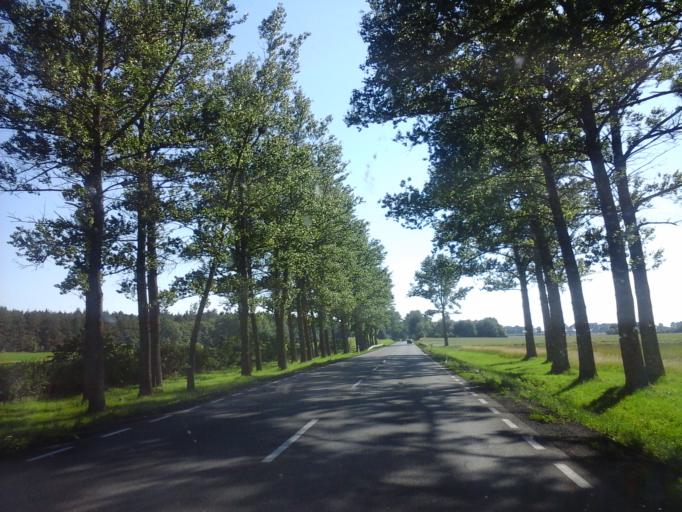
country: PL
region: West Pomeranian Voivodeship
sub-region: Powiat gryficki
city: Brojce
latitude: 53.8658
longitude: 15.3567
